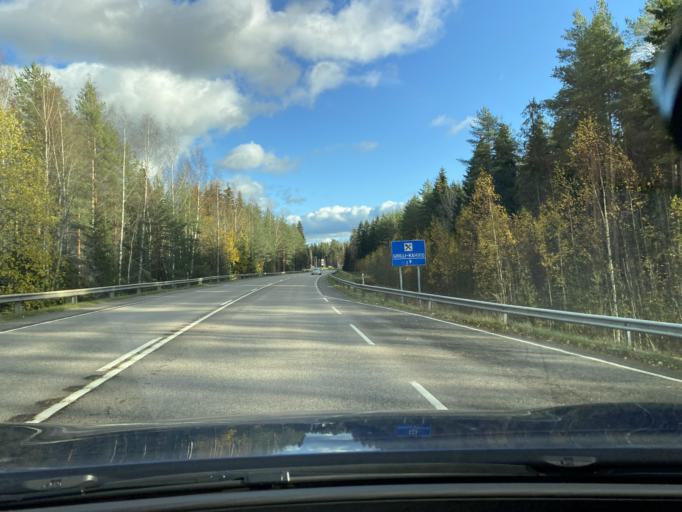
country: FI
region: Haeme
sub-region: Riihimaeki
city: Oitti
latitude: 60.7927
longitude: 24.9888
